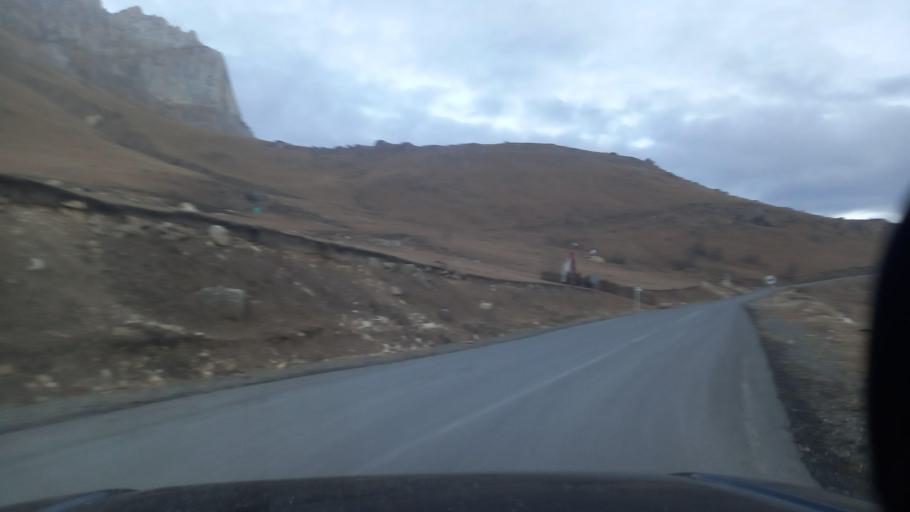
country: RU
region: Ingushetiya
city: Dzhayrakh
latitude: 42.8251
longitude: 44.8241
